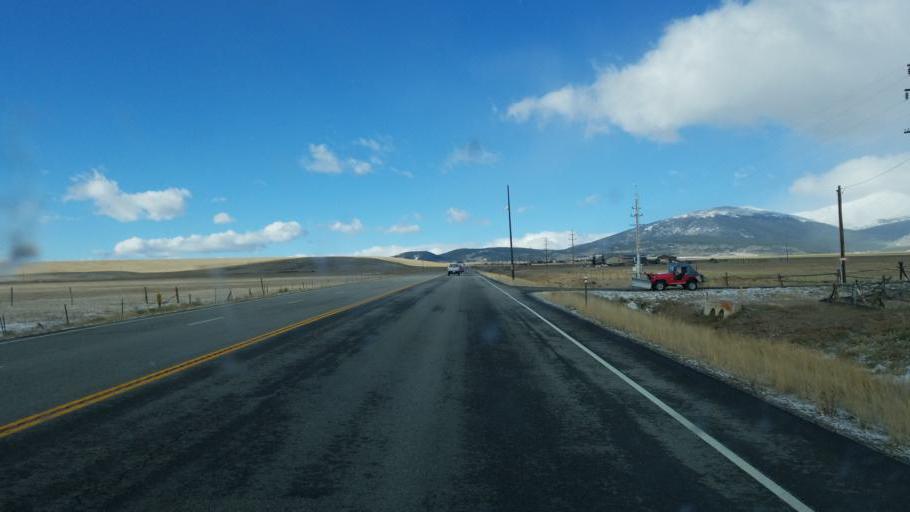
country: US
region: Colorado
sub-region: Park County
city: Fairplay
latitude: 39.3454
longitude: -105.8428
